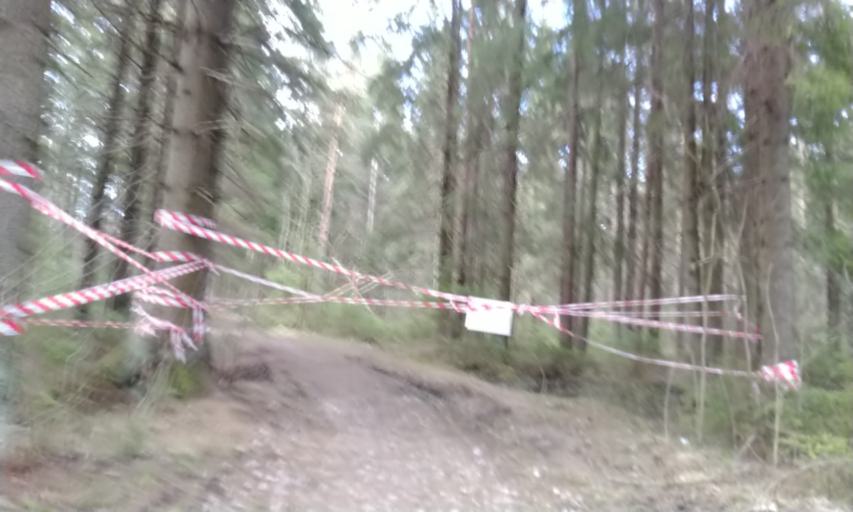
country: RU
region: Leningrad
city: Toksovo
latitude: 60.1317
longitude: 30.4518
